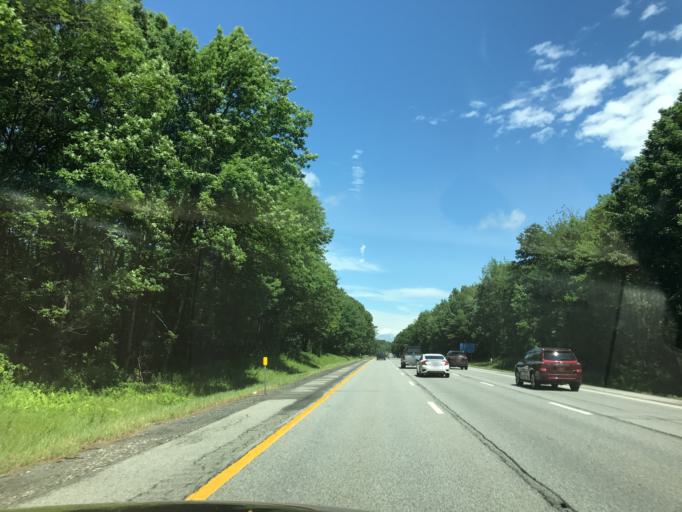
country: US
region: New York
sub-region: Saratoga County
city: Saratoga Springs
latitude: 43.1757
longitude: -73.7093
